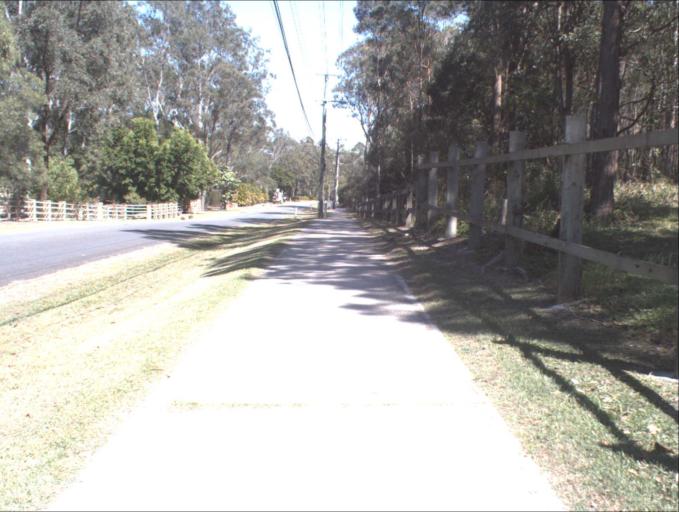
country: AU
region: Queensland
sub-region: Logan
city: Springwood
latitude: -27.6166
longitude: 153.1480
